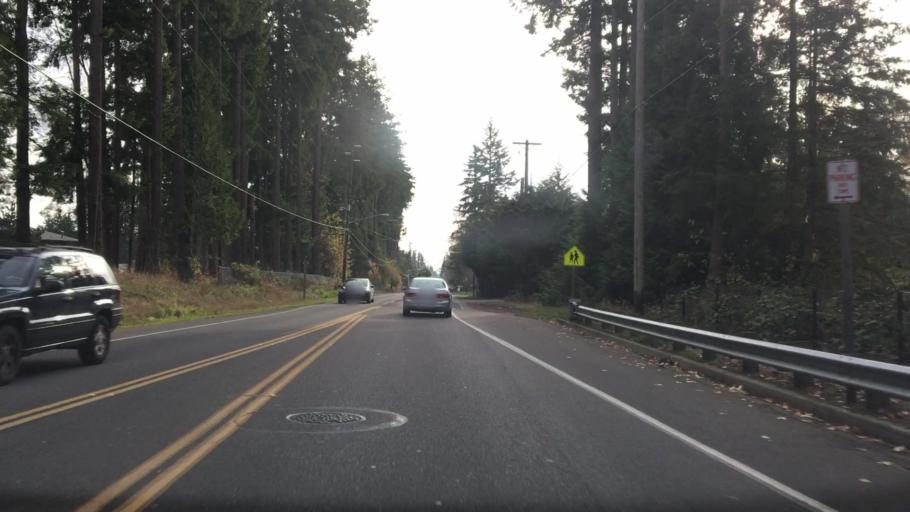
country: US
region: Washington
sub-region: Pierce County
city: South Hill
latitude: 47.1395
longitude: -122.3149
